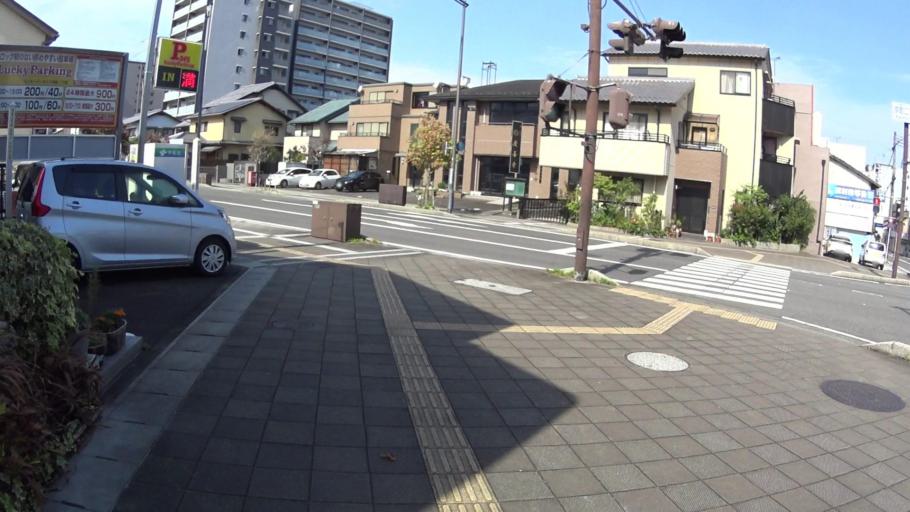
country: JP
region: Shiga Prefecture
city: Otsu-shi
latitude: 35.0069
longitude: 135.8452
